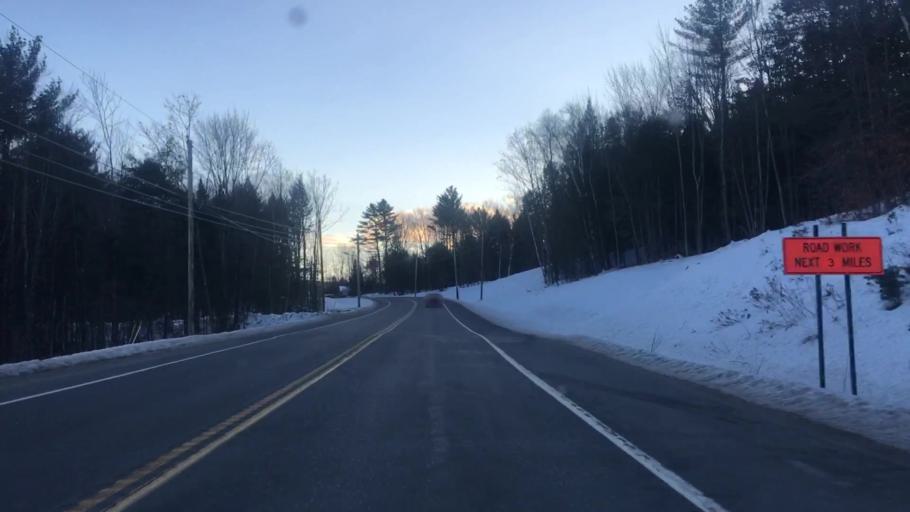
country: US
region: Maine
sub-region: Oxford County
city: Peru
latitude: 44.5254
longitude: -70.4076
